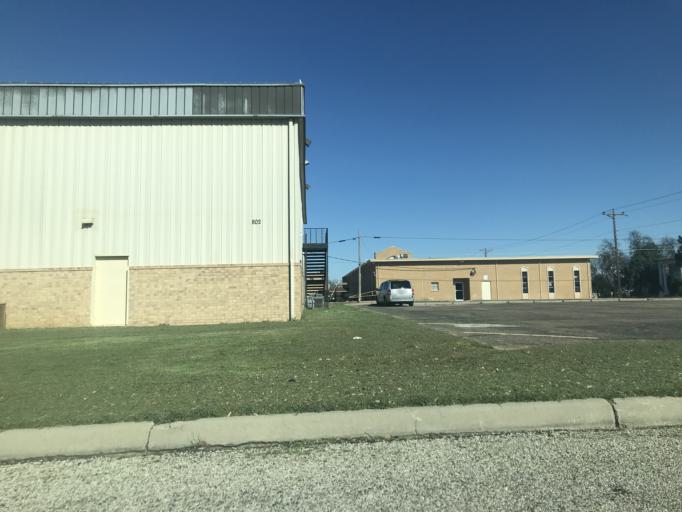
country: US
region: Texas
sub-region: Tom Green County
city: San Angelo
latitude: 31.4531
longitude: -100.4459
